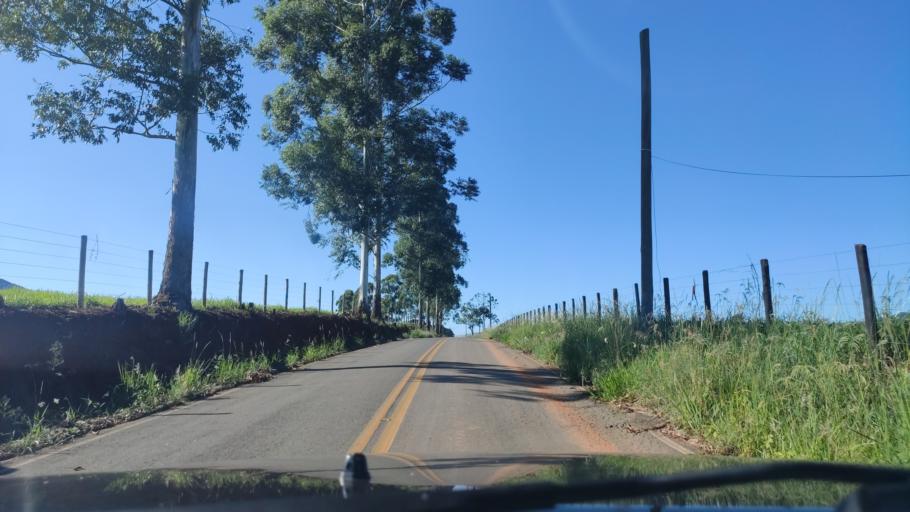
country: BR
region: Sao Paulo
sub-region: Serra Negra
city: Serra Negra
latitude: -22.5774
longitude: -46.6220
